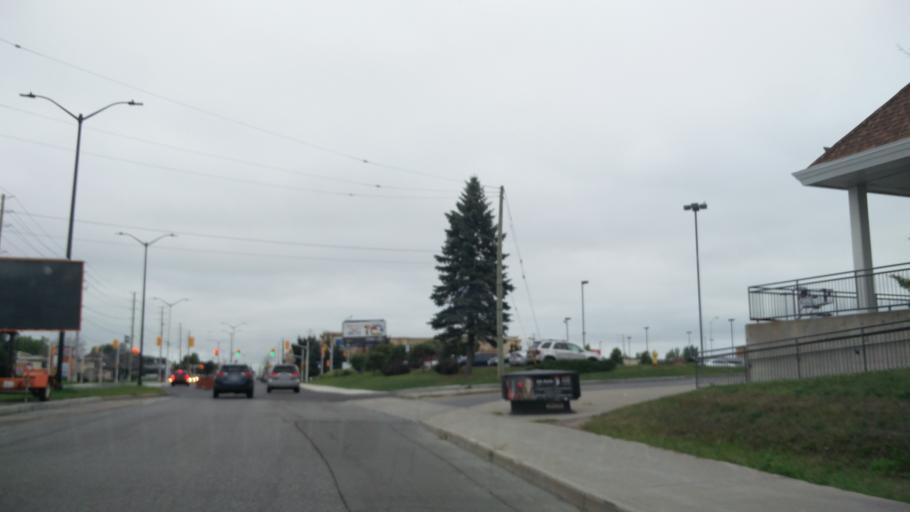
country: CA
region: Ontario
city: Bells Corners
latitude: 45.2677
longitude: -75.7447
